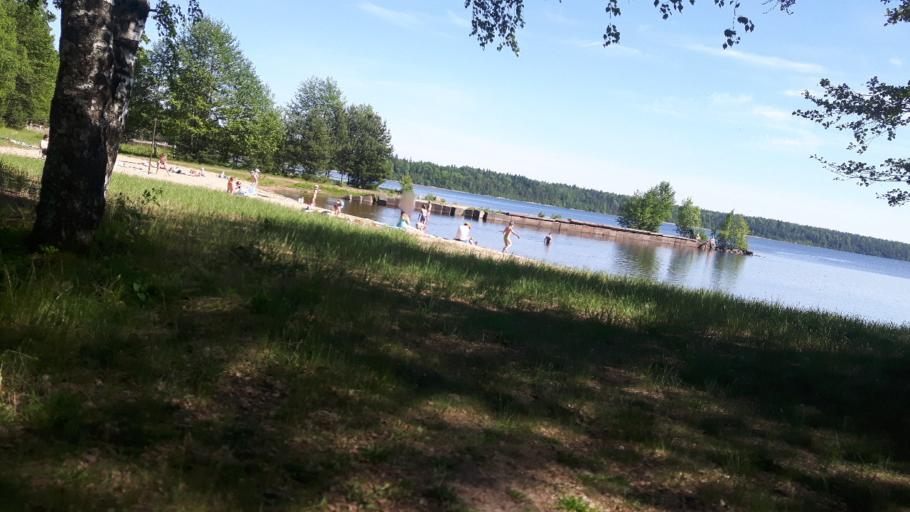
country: RU
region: Leningrad
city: Sista-Palkino
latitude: 59.7615
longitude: 28.7400
